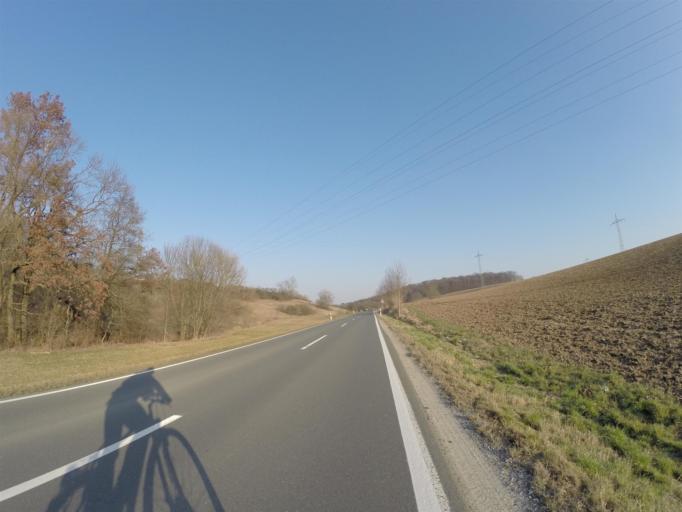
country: DE
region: Thuringia
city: Mellingen
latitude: 50.9402
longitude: 11.4101
